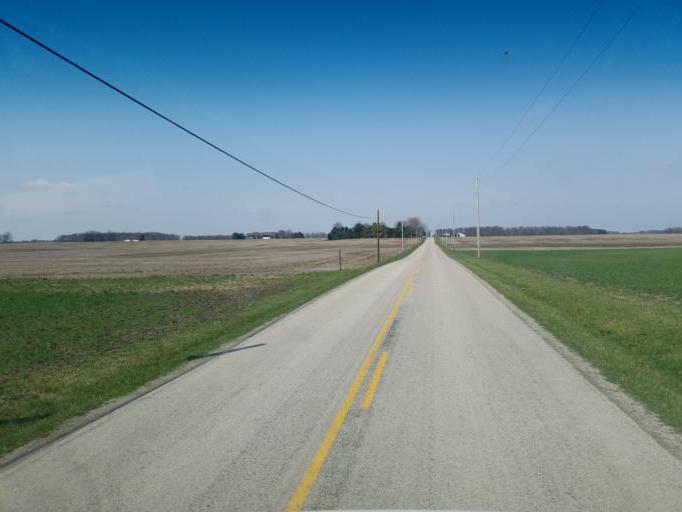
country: US
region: Ohio
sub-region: Wyandot County
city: Upper Sandusky
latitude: 40.8764
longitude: -83.2655
